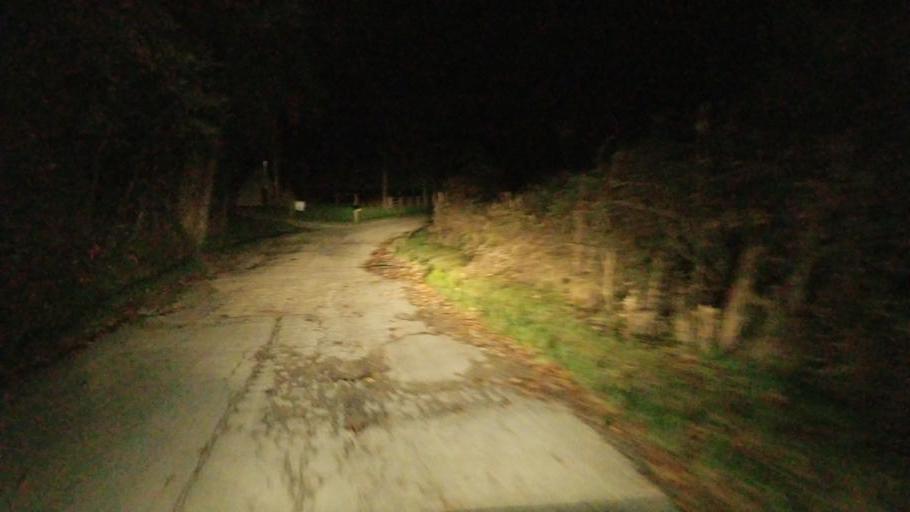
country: US
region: Ohio
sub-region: Belmont County
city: Barnesville
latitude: 40.1353
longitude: -81.2200
